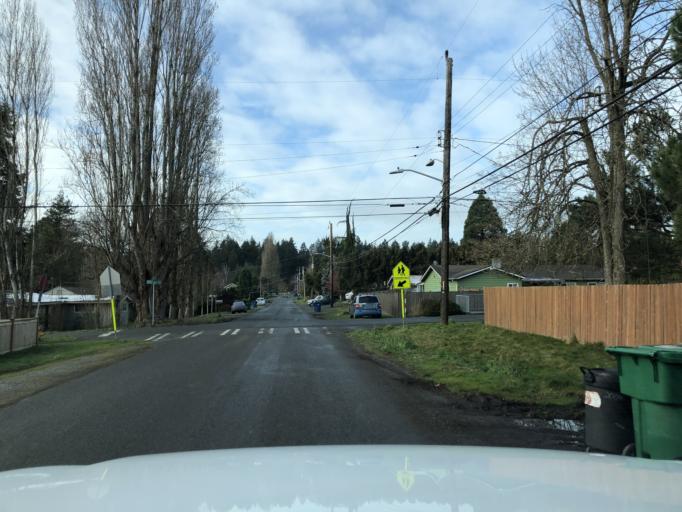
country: US
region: Washington
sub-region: King County
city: Lake Forest Park
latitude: 47.7284
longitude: -122.3068
